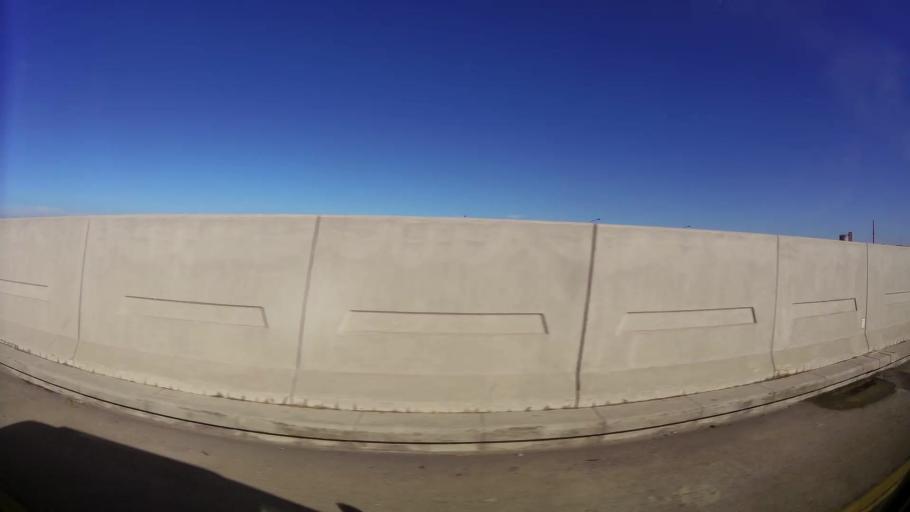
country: ZA
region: Eastern Cape
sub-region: Nelson Mandela Bay Metropolitan Municipality
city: Port Elizabeth
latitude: -33.9171
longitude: 25.6101
